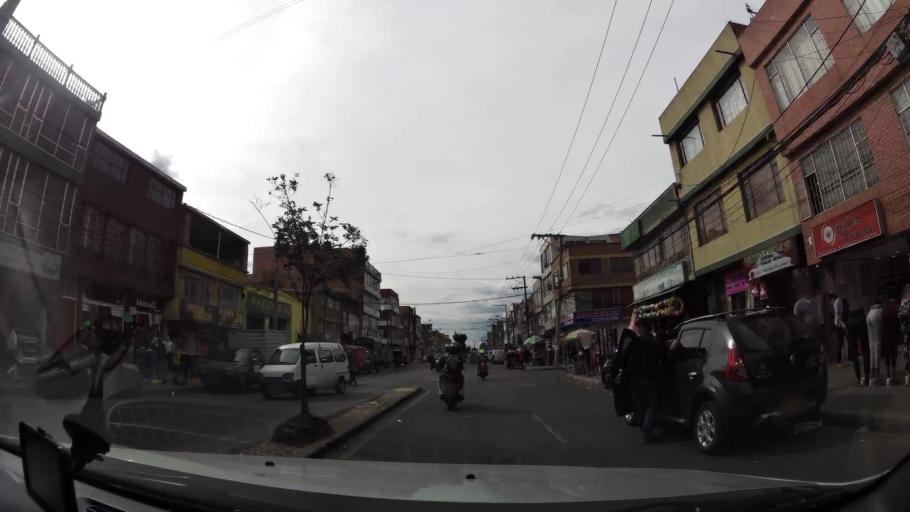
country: CO
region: Cundinamarca
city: Soacha
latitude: 4.6378
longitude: -74.1654
